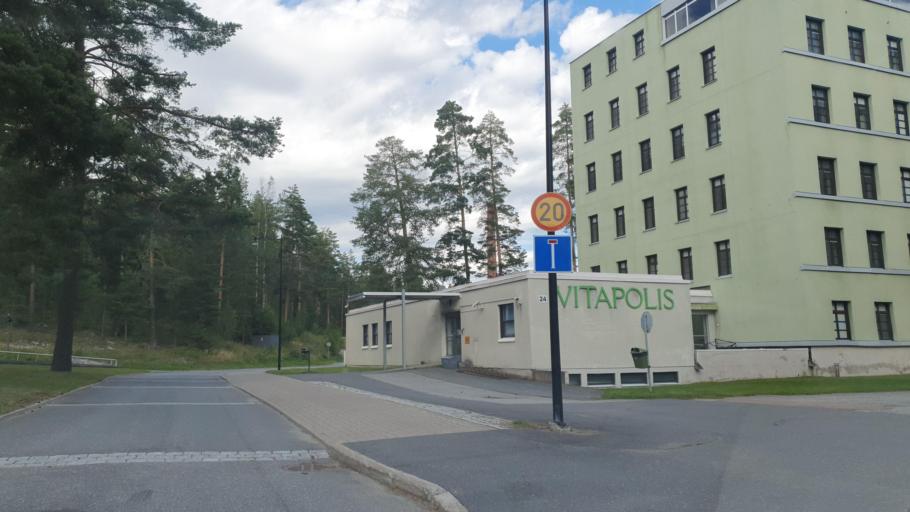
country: FI
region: Central Finland
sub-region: Jyvaeskylae
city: Saeynaetsalo
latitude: 62.1581
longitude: 25.7641
